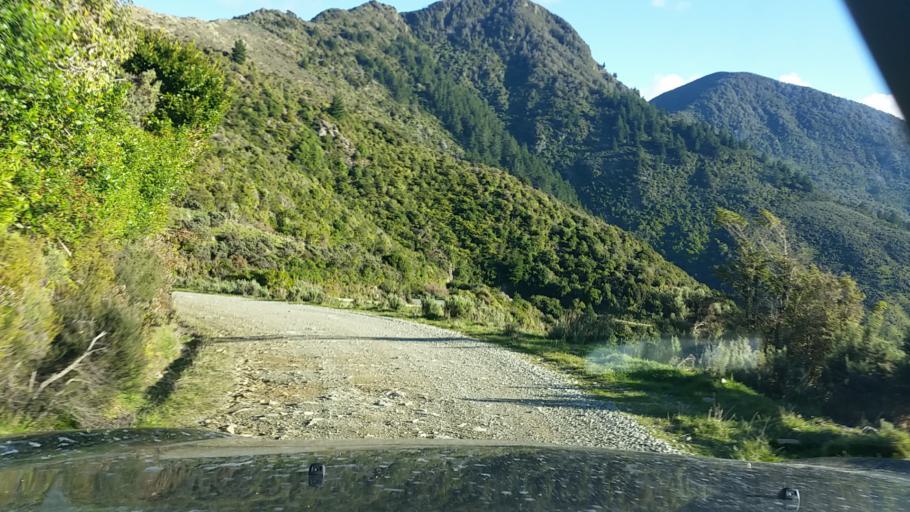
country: NZ
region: Marlborough
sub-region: Marlborough District
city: Picton
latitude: -41.0213
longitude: 174.1594
